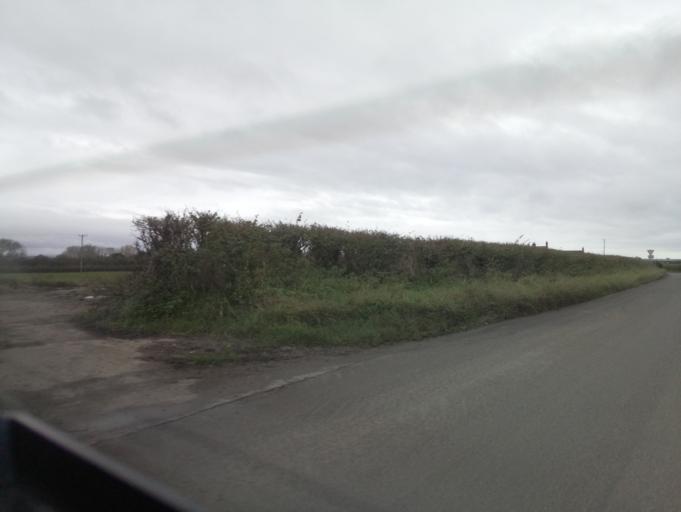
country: GB
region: England
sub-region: Somerset
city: Yeovil
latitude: 51.0027
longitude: -2.5932
